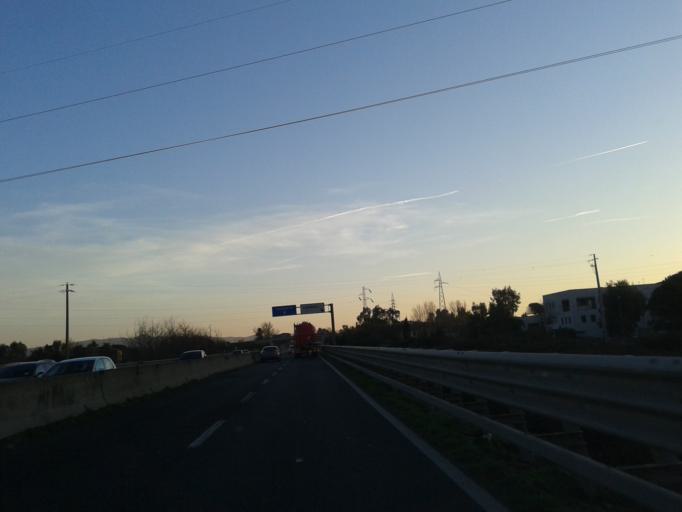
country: IT
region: Tuscany
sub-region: Provincia di Livorno
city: Livorno
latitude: 43.5650
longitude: 10.3464
